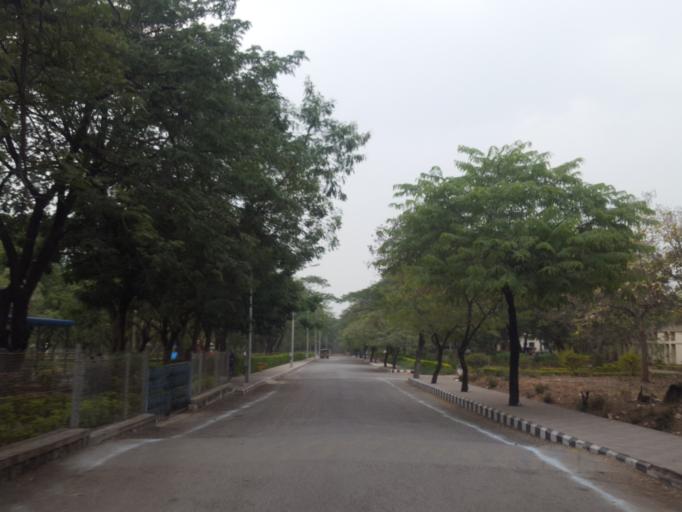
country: IN
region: Telangana
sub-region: Rangareddi
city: Singapur
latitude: 17.4688
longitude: 78.1647
